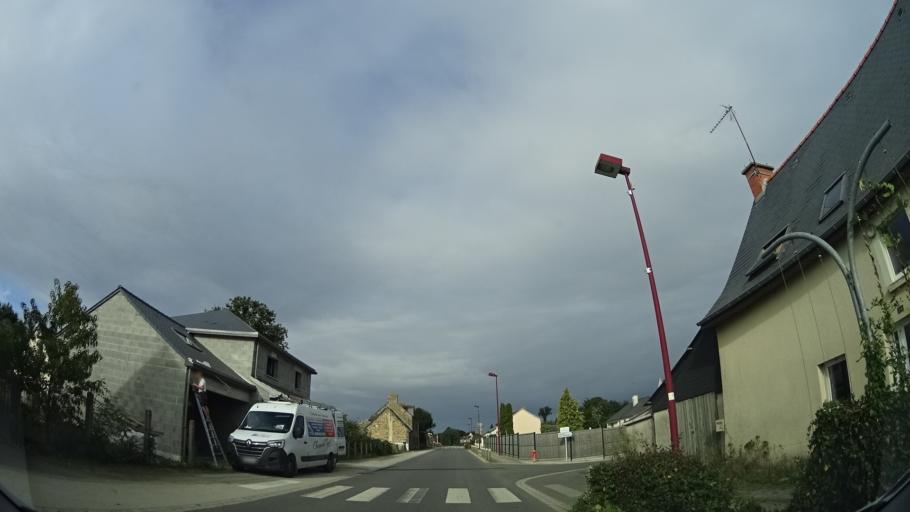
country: FR
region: Brittany
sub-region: Departement d'Ille-et-Vilaine
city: Guipel
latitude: 48.2985
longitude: -1.7274
